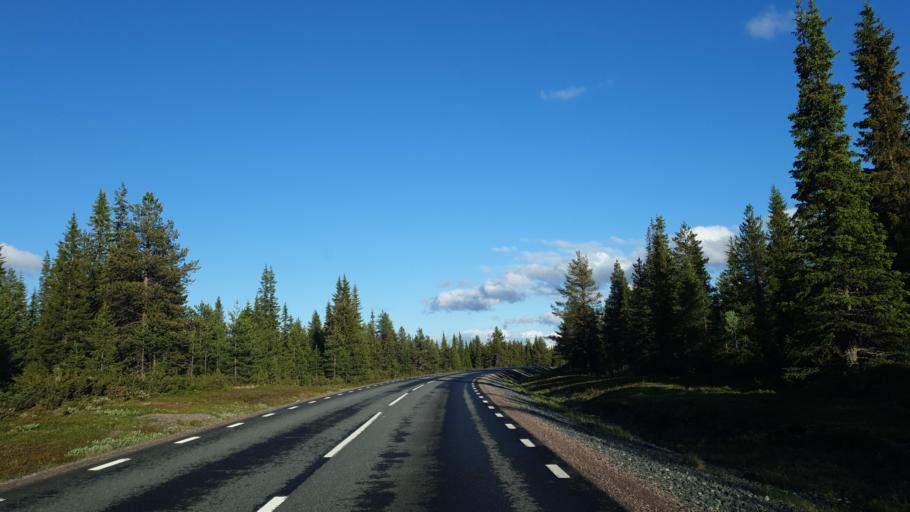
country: SE
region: Norrbotten
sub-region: Arjeplogs Kommun
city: Arjeplog
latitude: 65.9376
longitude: 18.2944
